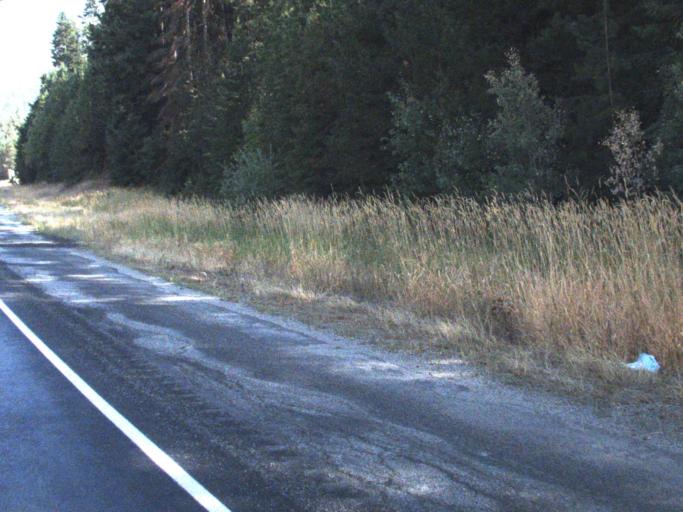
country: US
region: Washington
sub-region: Spokane County
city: Deer Park
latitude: 48.0982
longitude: -117.2960
